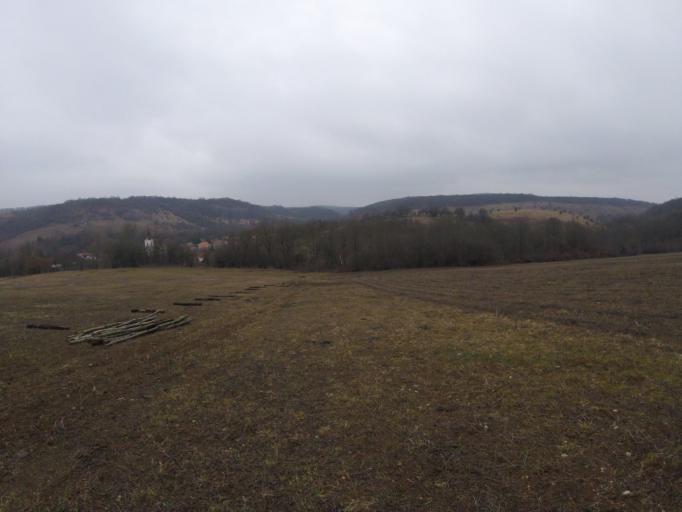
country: HU
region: Borsod-Abauj-Zemplen
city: Rudabanya
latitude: 48.4448
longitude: 20.5898
